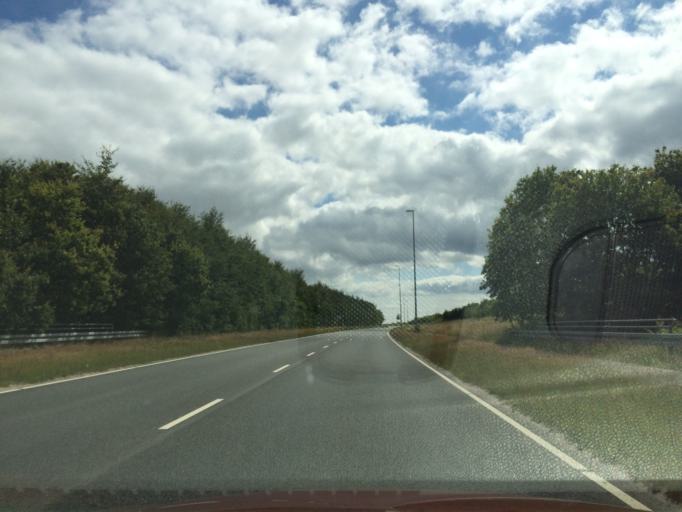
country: DK
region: Central Jutland
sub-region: Silkeborg Kommune
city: Silkeborg
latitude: 56.1936
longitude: 9.6050
